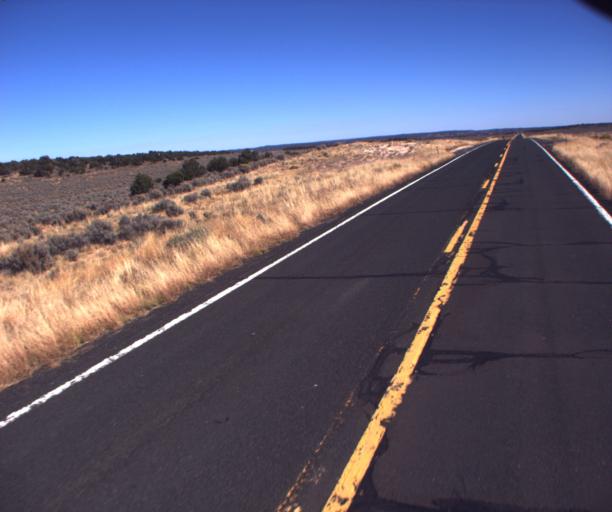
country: US
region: Arizona
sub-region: Navajo County
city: First Mesa
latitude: 35.7533
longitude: -110.0327
